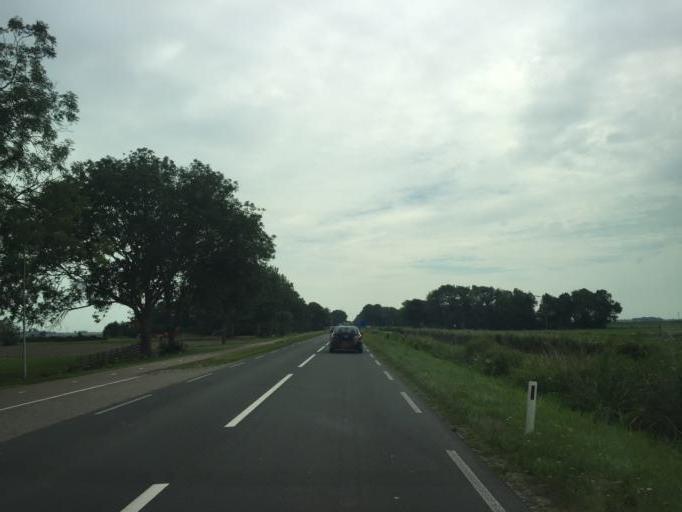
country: NL
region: North Holland
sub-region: Gemeente Alkmaar
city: Alkmaar
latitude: 52.6181
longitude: 4.7897
